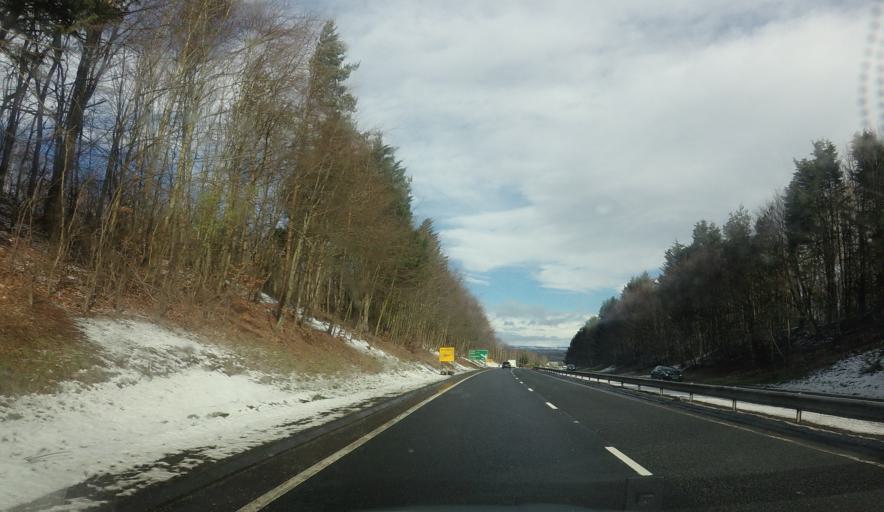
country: GB
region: Scotland
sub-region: Perth and Kinross
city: Perth
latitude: 56.3983
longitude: -3.4888
